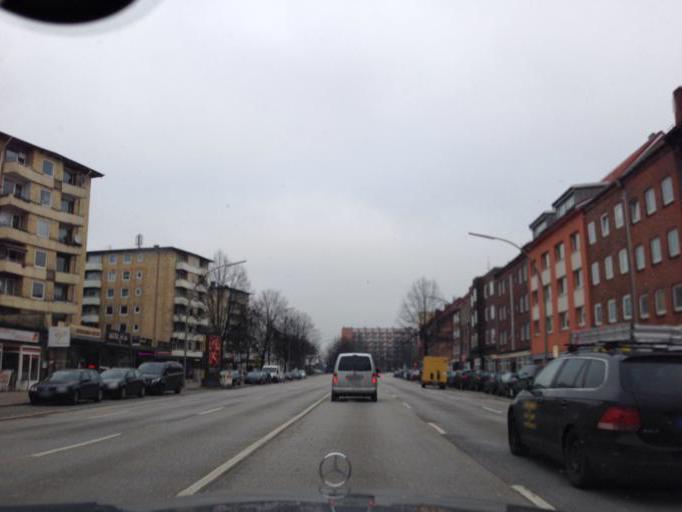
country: DE
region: Hamburg
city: Borgfelde
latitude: 53.5654
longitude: 10.0371
